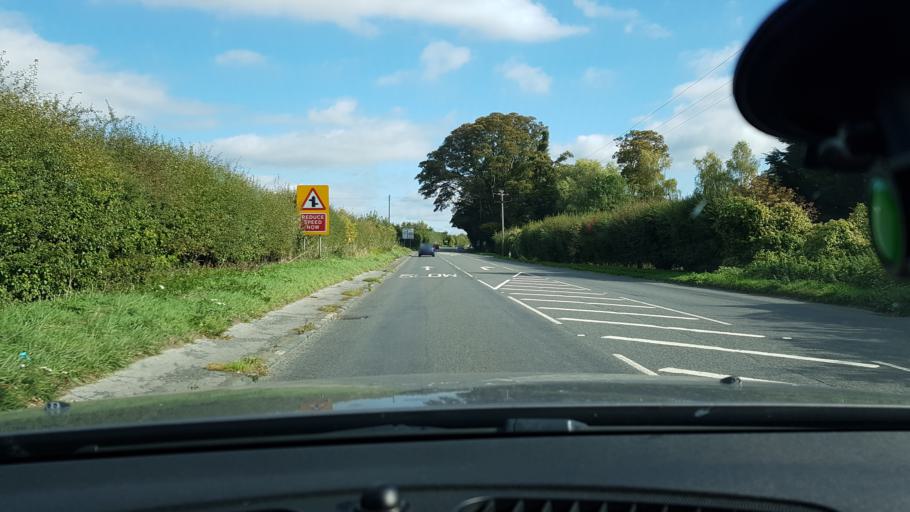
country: GB
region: England
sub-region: West Berkshire
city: Hungerford
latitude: 51.4160
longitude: -1.4978
